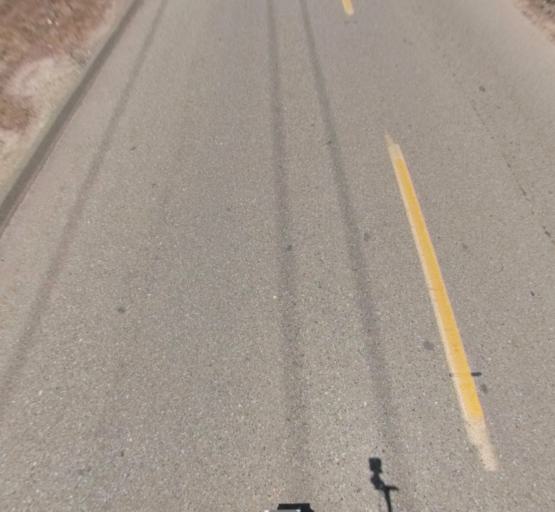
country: US
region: California
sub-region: Madera County
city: Chowchilla
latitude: 37.1613
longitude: -120.2020
